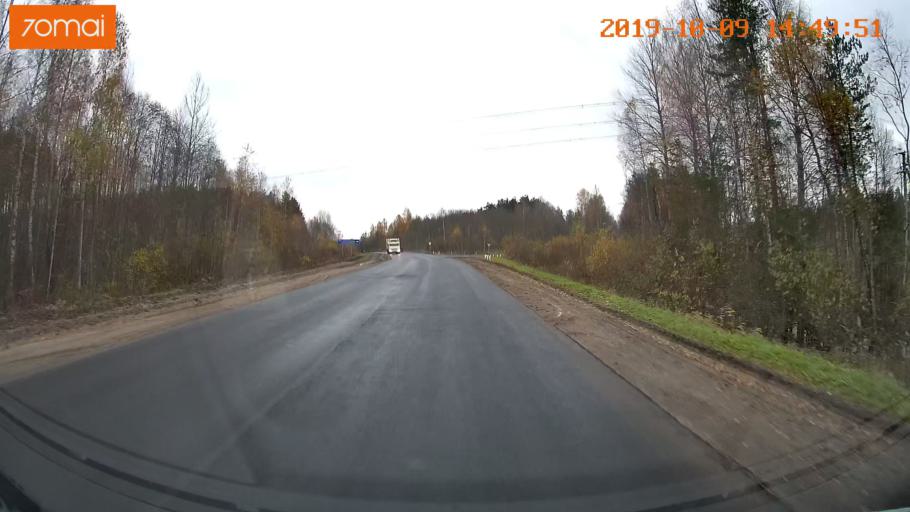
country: RU
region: Kostroma
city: Chistyye Bory
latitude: 58.3892
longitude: 41.5884
